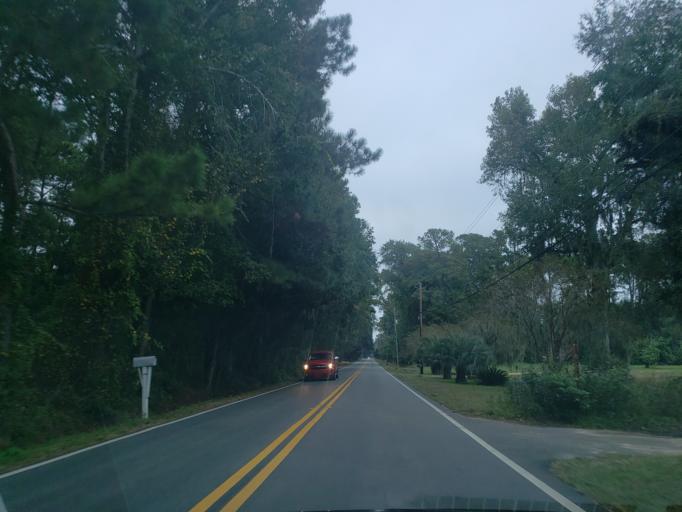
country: US
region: Georgia
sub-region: Chatham County
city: Montgomery
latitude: 31.9466
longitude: -81.1085
